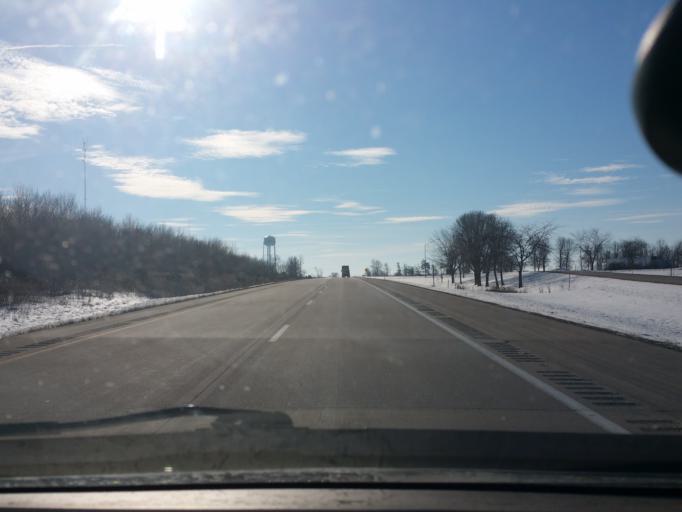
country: US
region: Iowa
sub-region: Clarke County
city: Osceola
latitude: 40.9941
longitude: -93.7993
